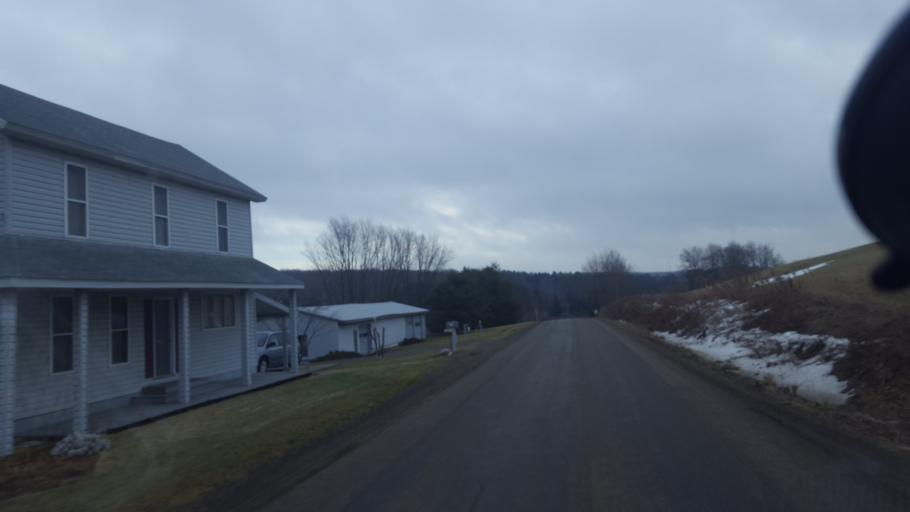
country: US
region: New York
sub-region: Allegany County
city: Andover
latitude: 41.9880
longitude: -77.7558
